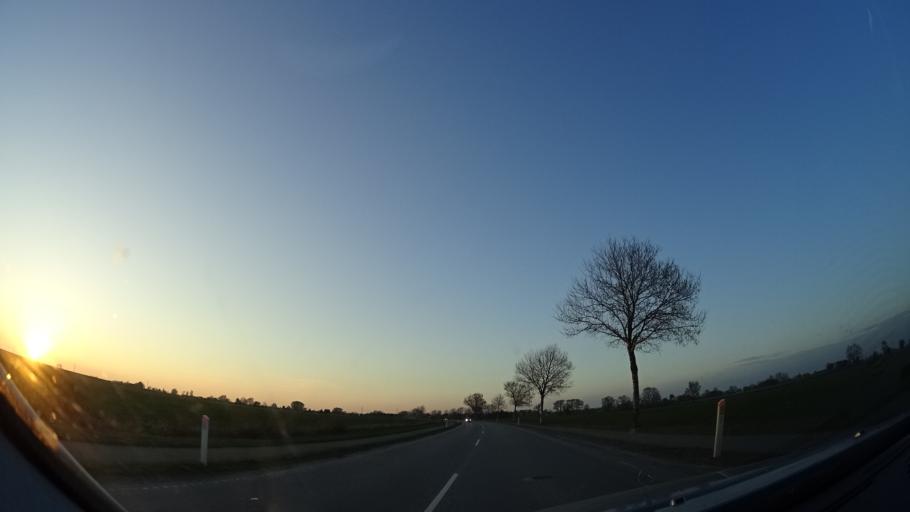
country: DK
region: Zealand
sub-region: Solrod Kommune
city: Solrod
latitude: 55.5280
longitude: 12.1823
